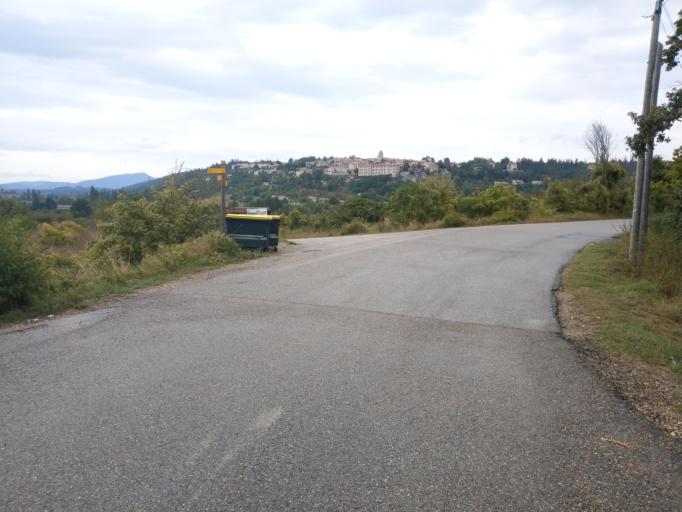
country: FR
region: Provence-Alpes-Cote d'Azur
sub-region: Departement du Vaucluse
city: Sault
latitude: 44.0866
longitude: 5.4008
